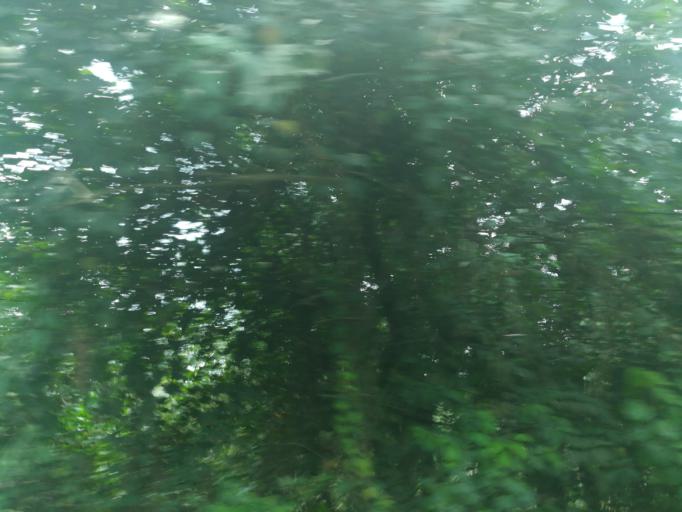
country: NG
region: Lagos
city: Ikorodu
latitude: 6.6745
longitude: 3.6525
